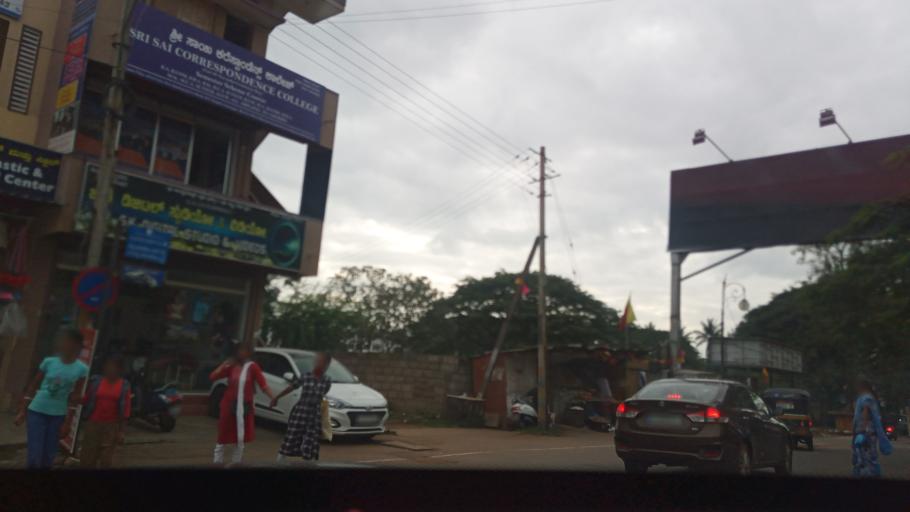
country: IN
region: Karnataka
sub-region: Mysore
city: Mysore
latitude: 12.2962
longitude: 76.6346
